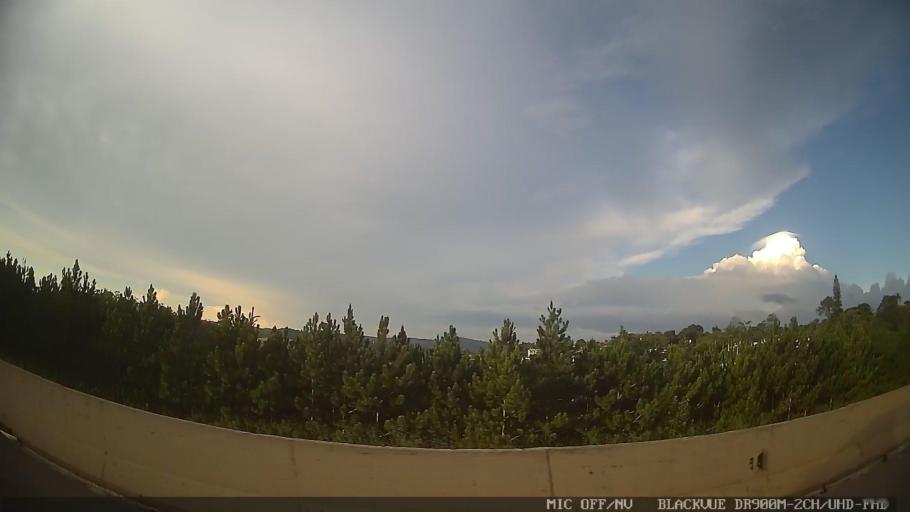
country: BR
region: Sao Paulo
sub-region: Itatiba
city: Itatiba
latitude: -23.0030
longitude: -46.7749
